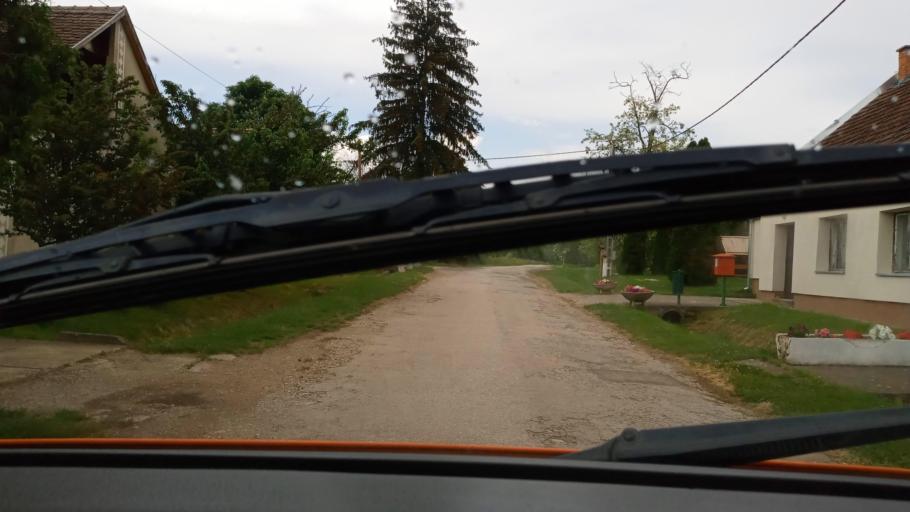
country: HU
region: Baranya
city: Harkany
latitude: 45.8998
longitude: 18.1367
